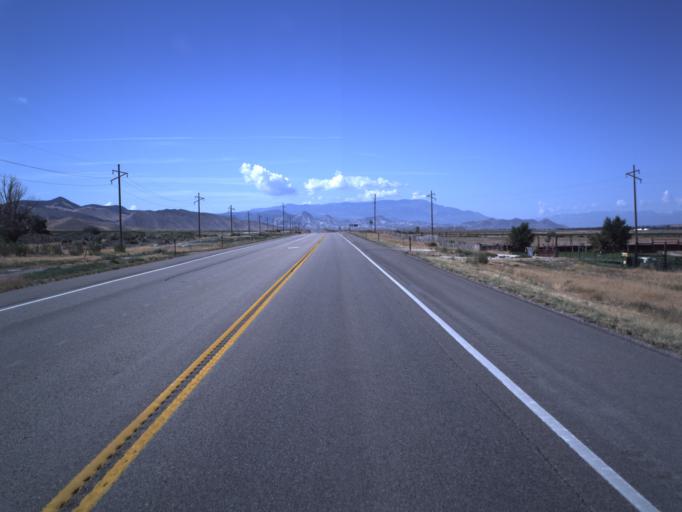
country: US
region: Utah
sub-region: Sanpete County
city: Centerfield
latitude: 39.0489
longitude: -111.8240
